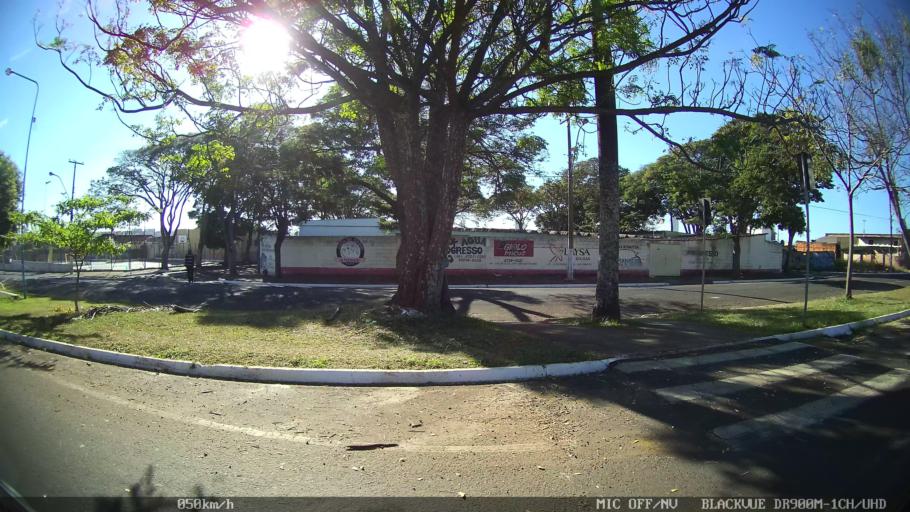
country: BR
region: Sao Paulo
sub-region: Franca
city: Franca
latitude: -20.5610
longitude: -47.3951
